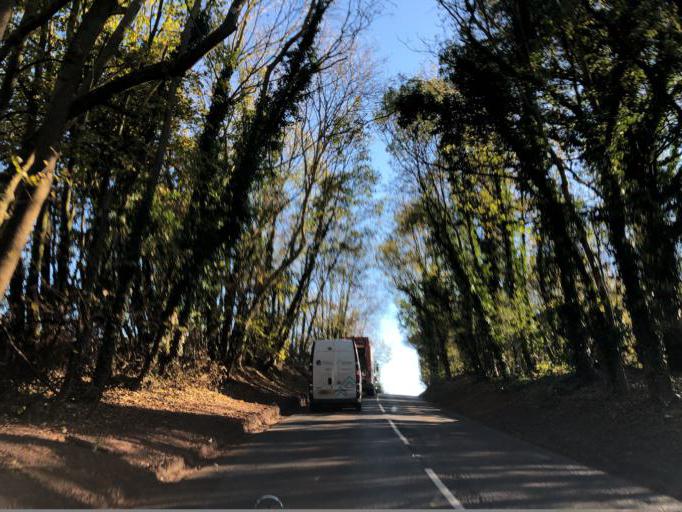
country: GB
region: England
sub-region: Warwickshire
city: Royal Leamington Spa
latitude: 52.2594
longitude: -1.5318
